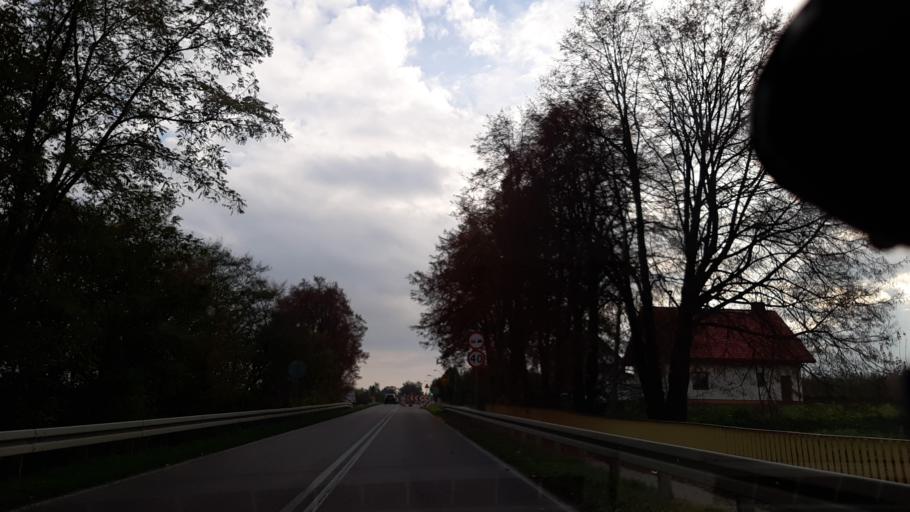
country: PL
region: Lublin Voivodeship
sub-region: Powiat pulawski
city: Naleczow
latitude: 51.3117
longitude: 22.2207
